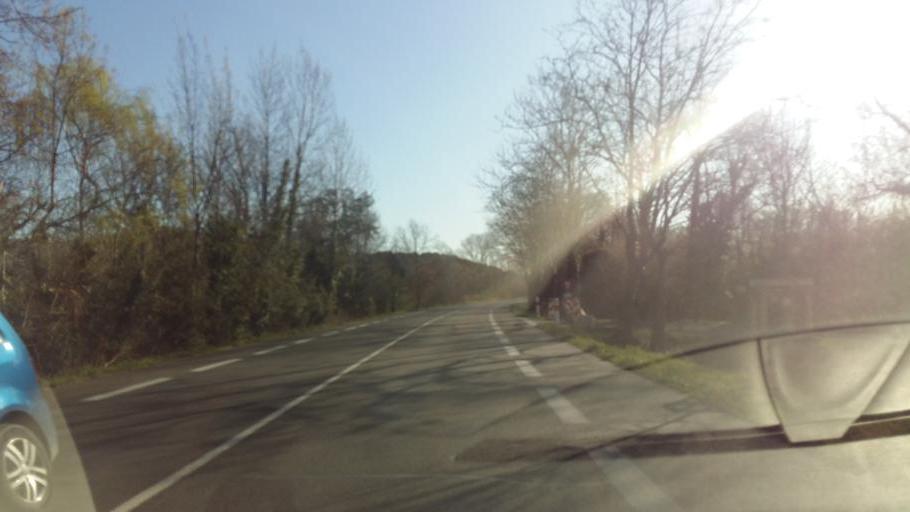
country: FR
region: Provence-Alpes-Cote d'Azur
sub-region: Departement du Vaucluse
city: Lauris
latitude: 43.7441
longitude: 5.3220
